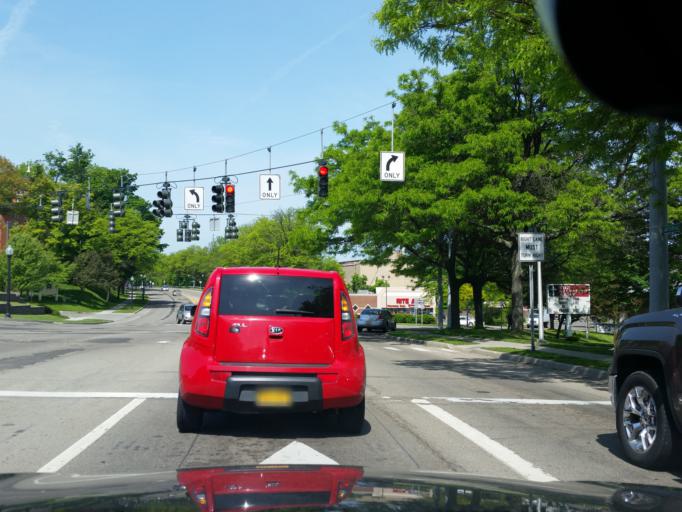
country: US
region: New York
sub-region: Chautauqua County
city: Jamestown
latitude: 42.0919
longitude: -79.2367
